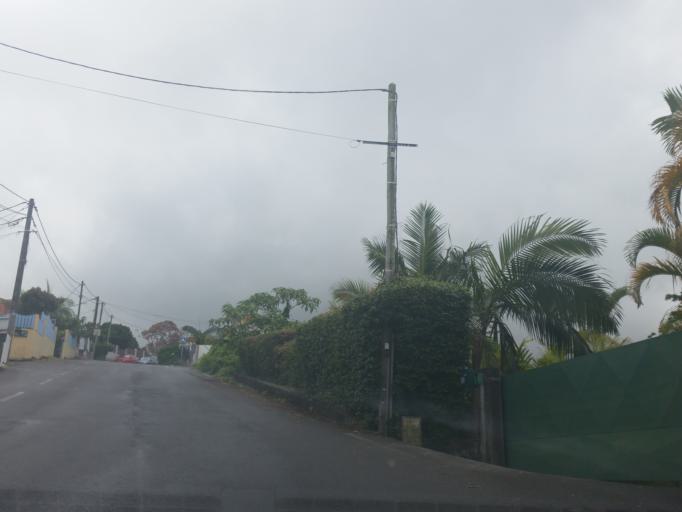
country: RE
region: Reunion
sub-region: Reunion
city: Le Tampon
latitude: -21.2425
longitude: 55.5139
